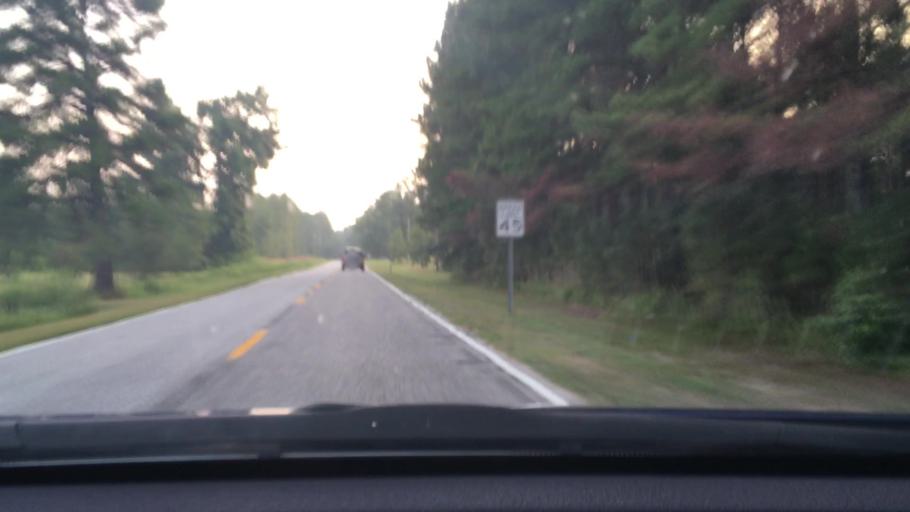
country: US
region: South Carolina
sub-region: Darlington County
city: Hartsville
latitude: 34.3274
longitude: -80.1043
